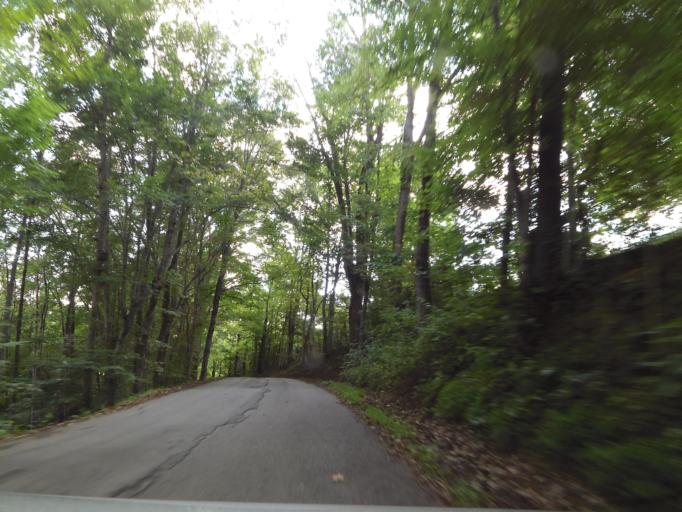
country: US
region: Tennessee
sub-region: Knox County
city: Mascot
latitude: 36.0970
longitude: -83.7735
